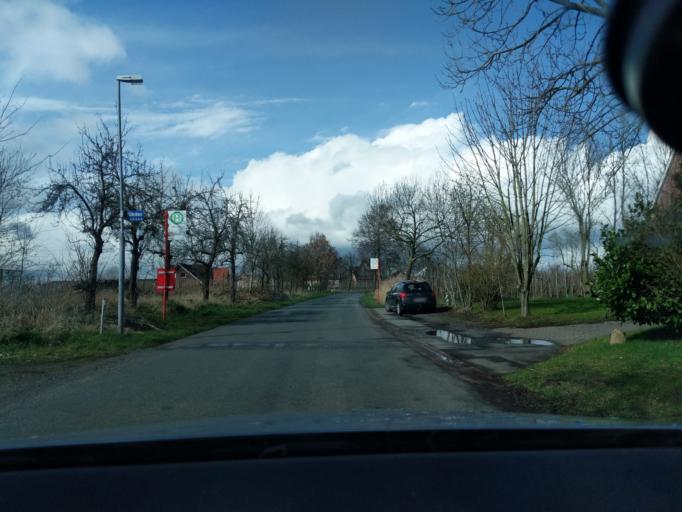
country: DE
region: Lower Saxony
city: Stade
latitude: 53.6076
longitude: 9.5203
